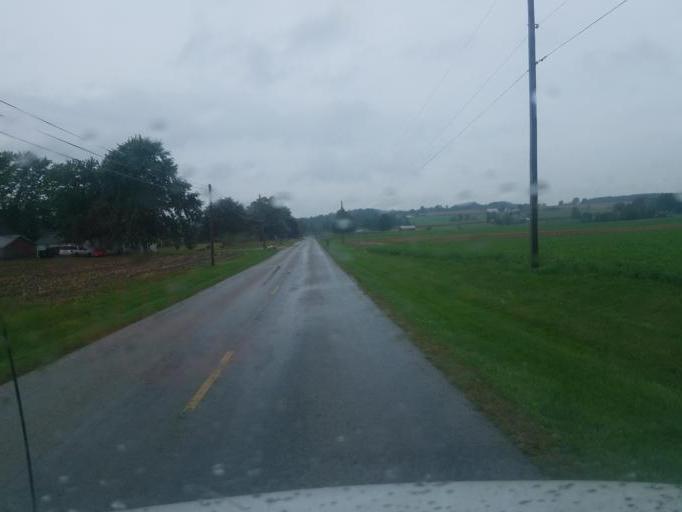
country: US
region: Ohio
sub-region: Wayne County
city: Rittman
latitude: 40.9843
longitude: -81.8071
